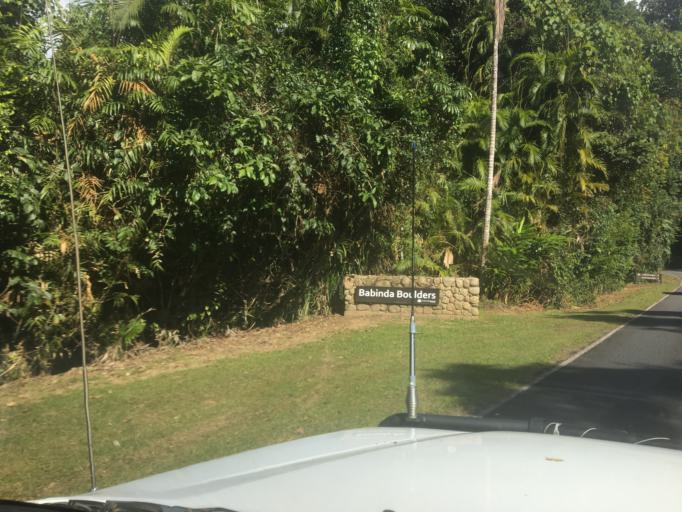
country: AU
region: Queensland
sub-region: Cassowary Coast
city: Innisfail
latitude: -17.3410
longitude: 145.8713
